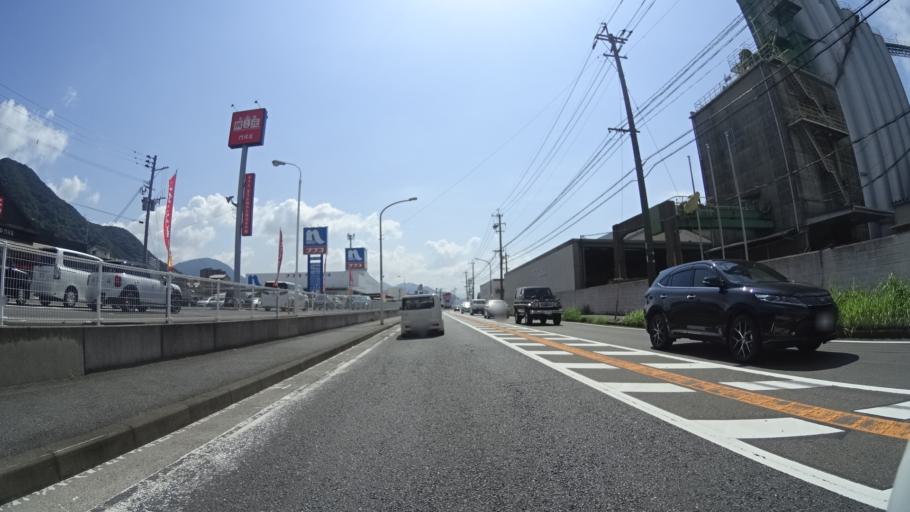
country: JP
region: Yamaguchi
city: Shimonoseki
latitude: 33.9335
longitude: 130.9446
